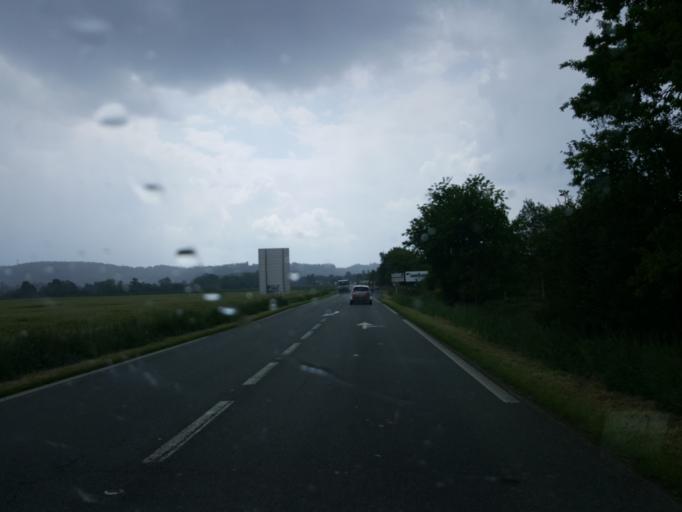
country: FR
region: Picardie
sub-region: Departement de l'Oise
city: Auneuil
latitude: 49.3881
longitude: 2.0054
